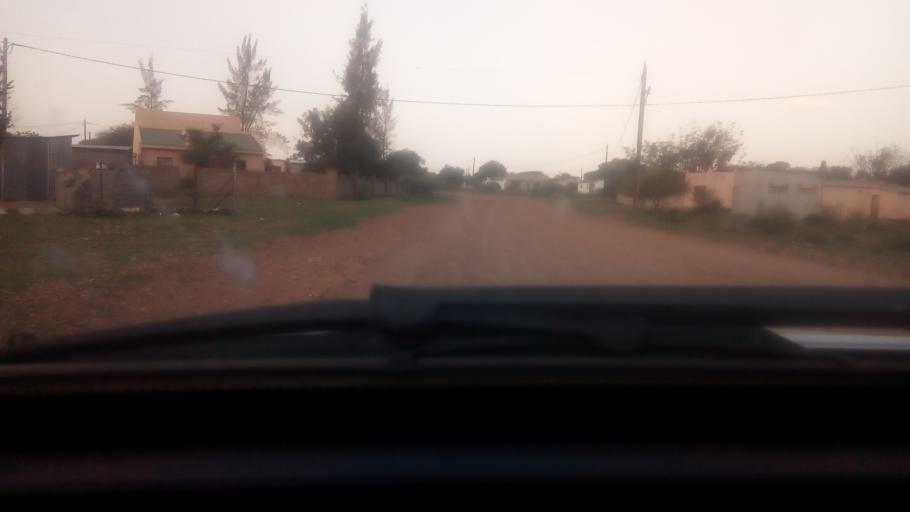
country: BW
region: Kgatleng
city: Bokaa
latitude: -24.4288
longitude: 26.0135
